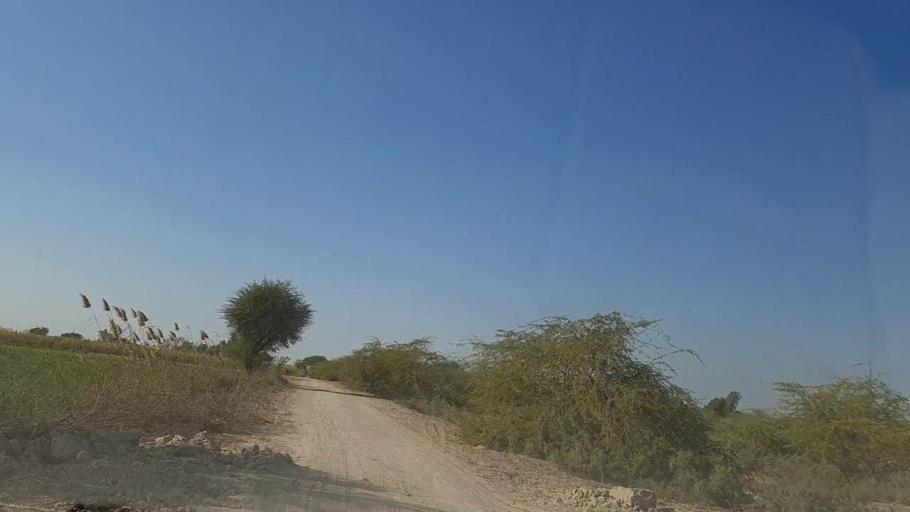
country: PK
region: Sindh
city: Digri
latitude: 25.1930
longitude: 68.9947
